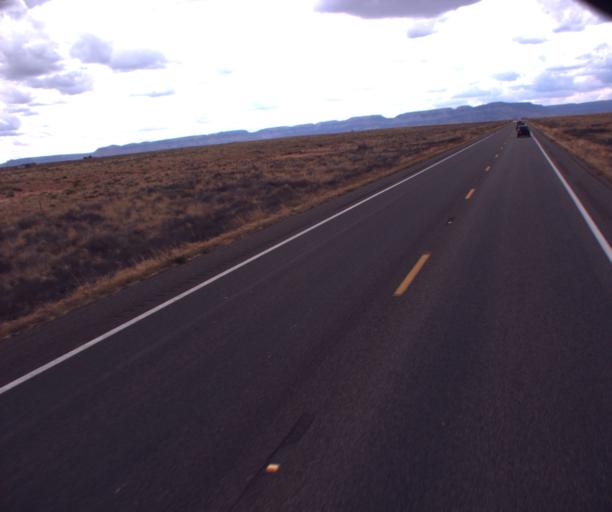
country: US
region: Arizona
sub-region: Navajo County
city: Kayenta
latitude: 36.7386
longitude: -110.0856
